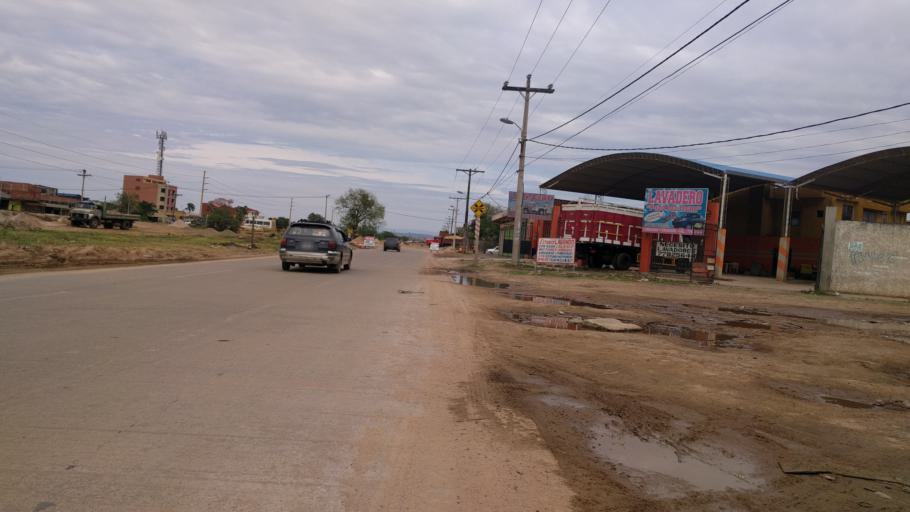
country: BO
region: Santa Cruz
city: Santa Cruz de la Sierra
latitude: -17.8415
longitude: -63.1726
